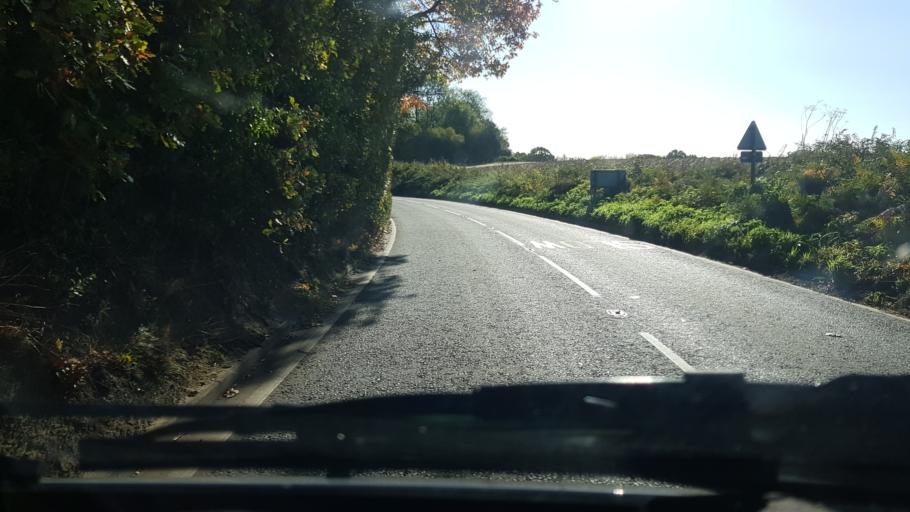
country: GB
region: England
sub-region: Surrey
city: Chilworth
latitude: 51.1791
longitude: -0.5226
